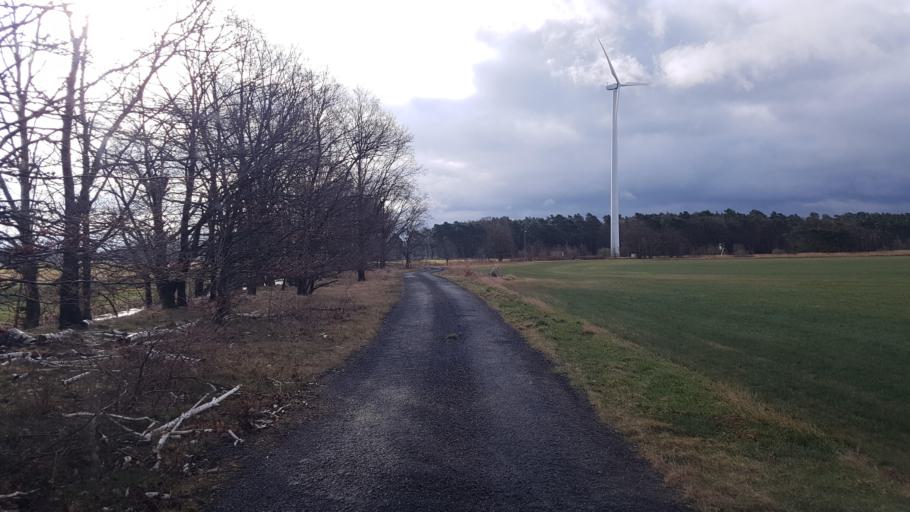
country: DE
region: Brandenburg
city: Bronkow
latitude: 51.6495
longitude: 13.8825
